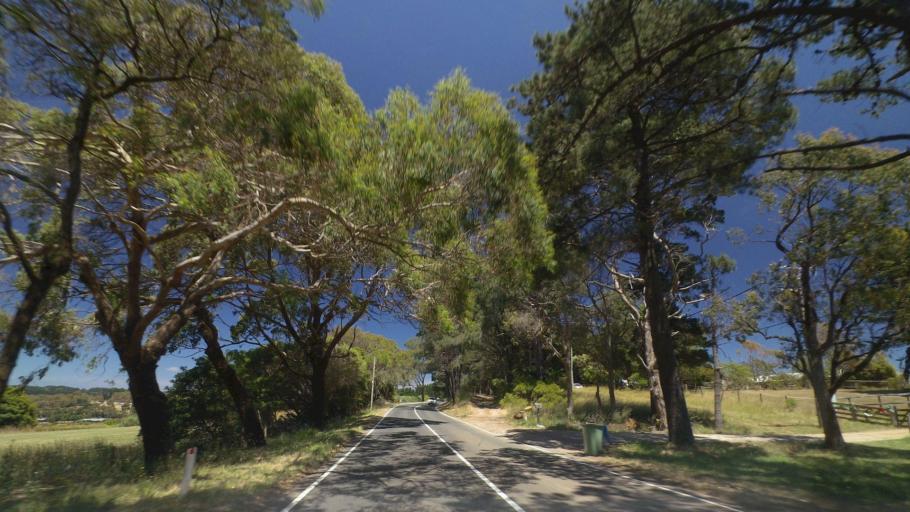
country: AU
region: Victoria
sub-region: Mornington Peninsula
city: Dromana
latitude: -38.3759
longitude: 144.9766
